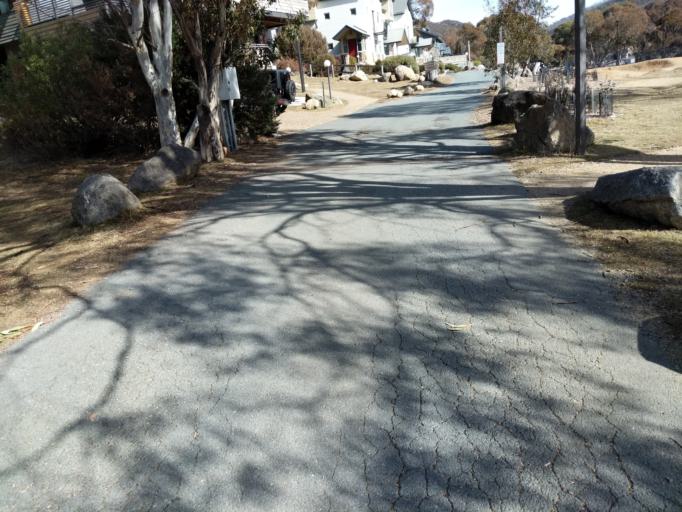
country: AU
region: New South Wales
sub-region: Snowy River
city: Jindabyne
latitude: -36.5053
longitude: 148.3036
